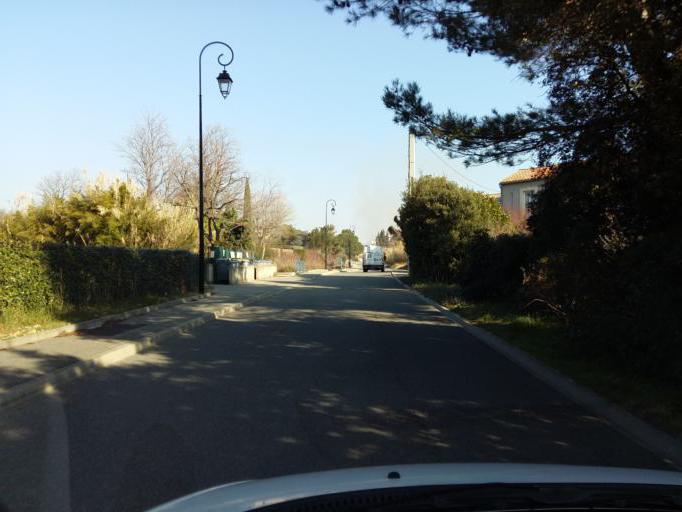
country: FR
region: Provence-Alpes-Cote d'Azur
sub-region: Departement du Vaucluse
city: Vaison-la-Romaine
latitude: 44.2483
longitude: 5.0180
